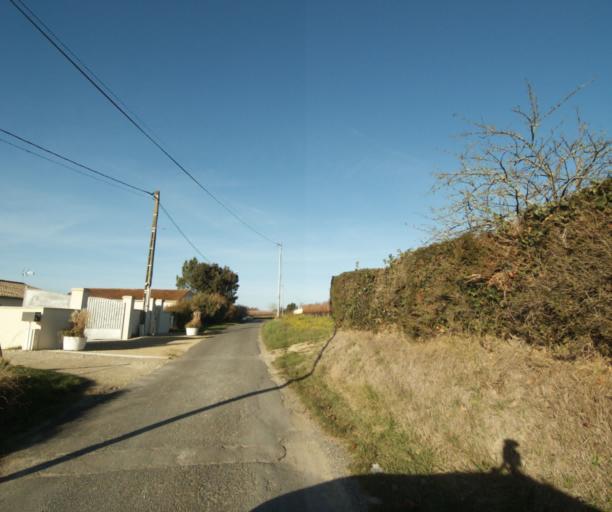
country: FR
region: Poitou-Charentes
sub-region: Departement de la Charente-Maritime
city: Cherac
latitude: 45.7070
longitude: -0.4518
